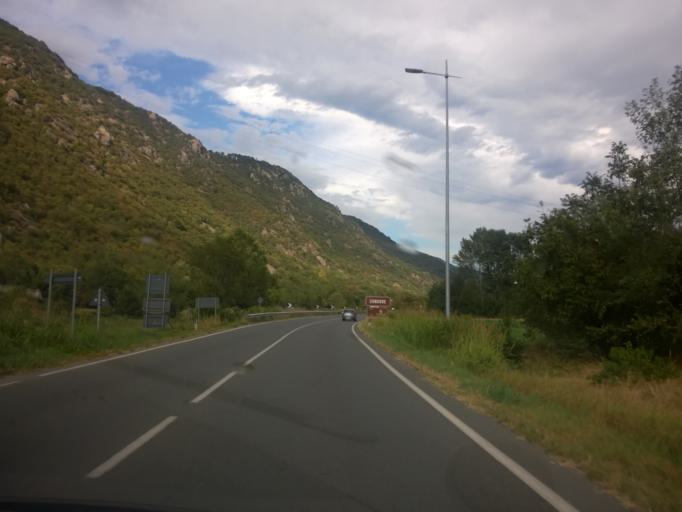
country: IT
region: Piedmont
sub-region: Provincia di Torino
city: Sant'Antonino di Susa
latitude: 45.1164
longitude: 7.2748
